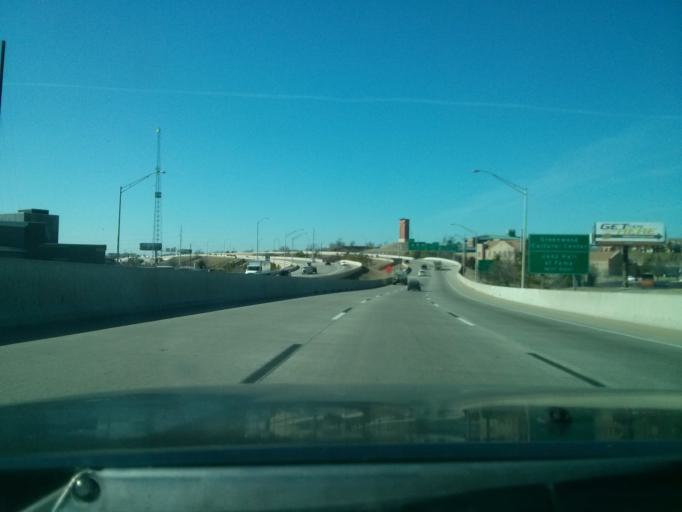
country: US
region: Oklahoma
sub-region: Tulsa County
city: Tulsa
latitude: 36.1611
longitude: -95.9870
